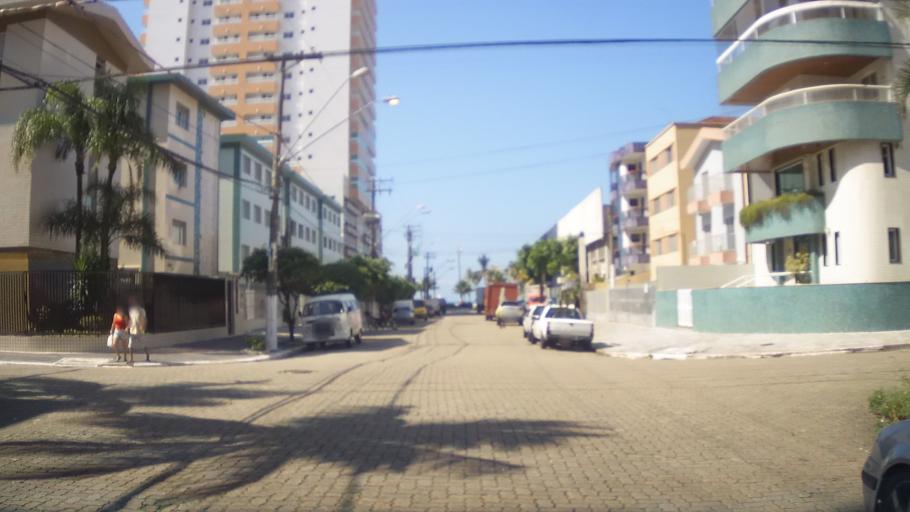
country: BR
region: Sao Paulo
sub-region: Praia Grande
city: Praia Grande
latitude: -24.0120
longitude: -46.4185
